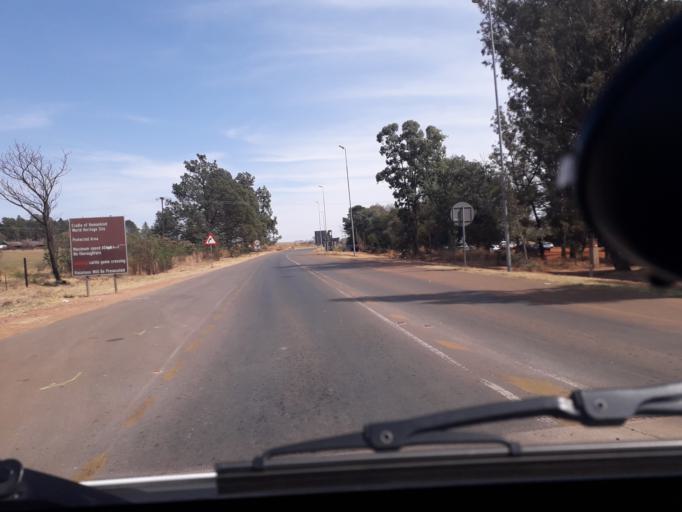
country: ZA
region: Gauteng
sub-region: West Rand District Municipality
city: Muldersdriseloop
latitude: -25.9876
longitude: 27.8186
